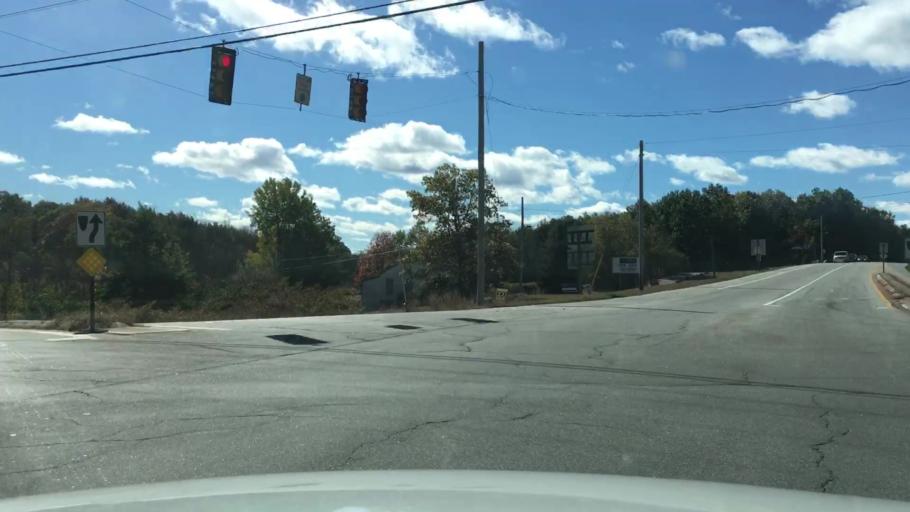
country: US
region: Maine
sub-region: York County
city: Alfred
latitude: 43.4709
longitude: -70.7200
